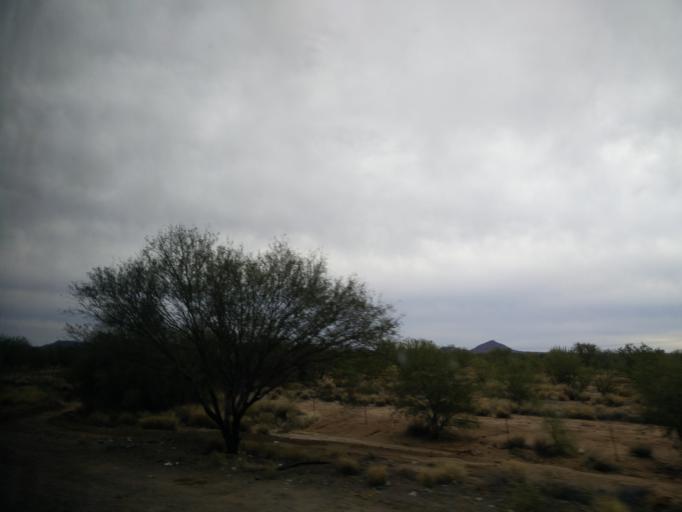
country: MX
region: Sonora
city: Hermosillo
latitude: 28.7184
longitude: -110.9818
